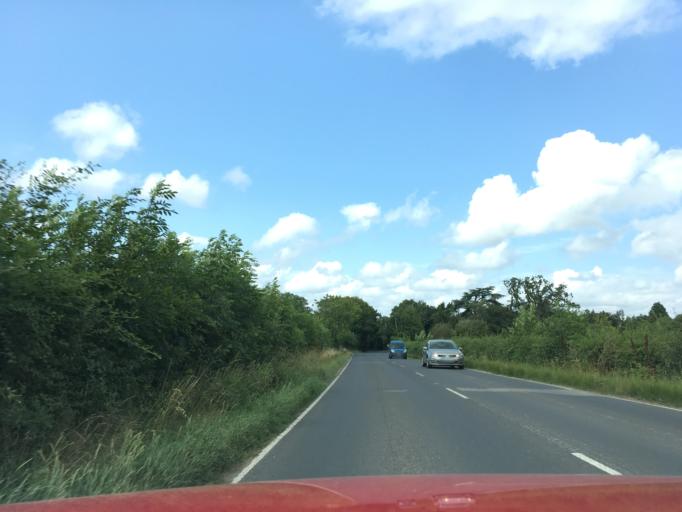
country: GB
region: England
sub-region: Kent
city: Tenterden
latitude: 51.1074
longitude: 0.6452
